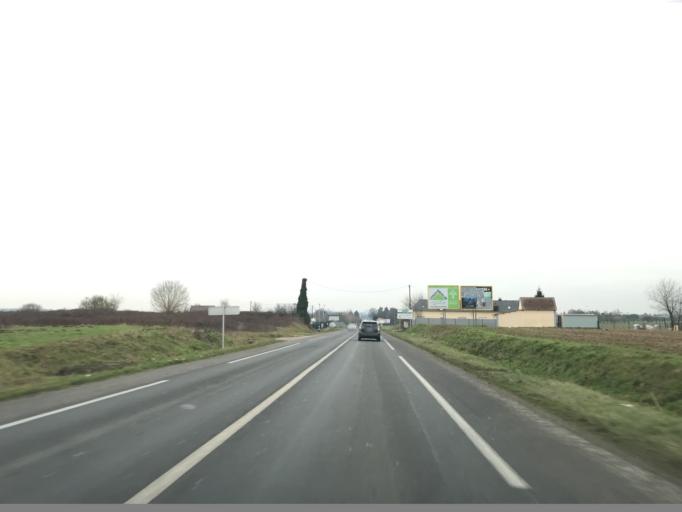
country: FR
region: Haute-Normandie
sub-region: Departement de la Seine-Maritime
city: Boos
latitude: 49.3923
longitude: 1.1926
